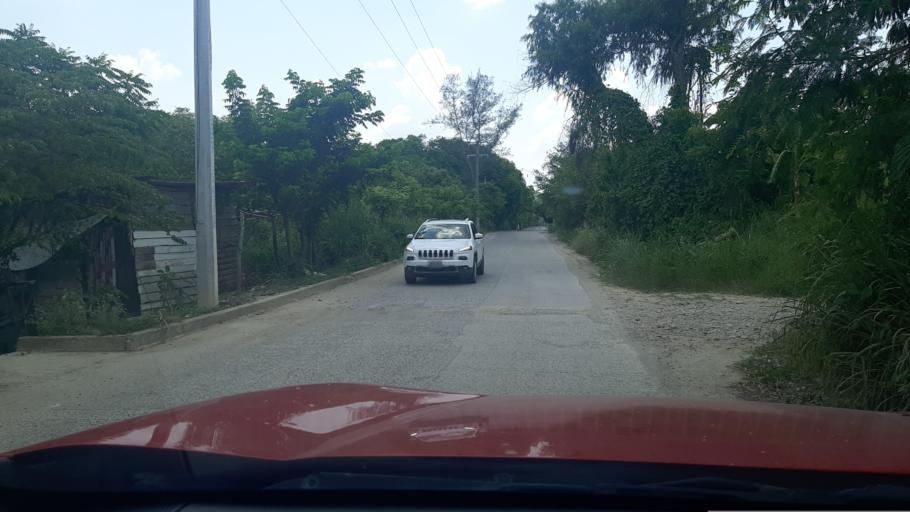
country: MX
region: Veracruz
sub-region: Poza Rica de Hidalgo
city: Arroyo del Maiz Uno
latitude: 20.4989
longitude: -97.4277
